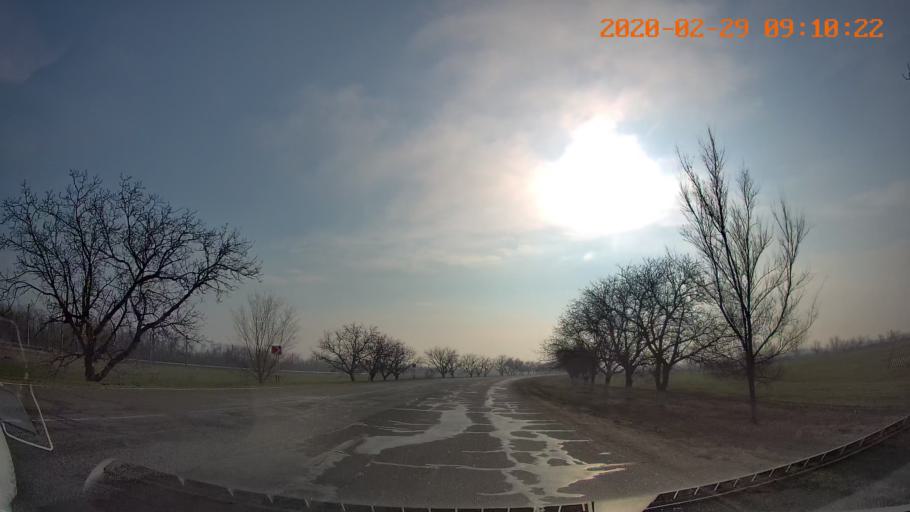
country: MD
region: Telenesti
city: Slobozia
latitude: 46.8445
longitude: 29.7807
